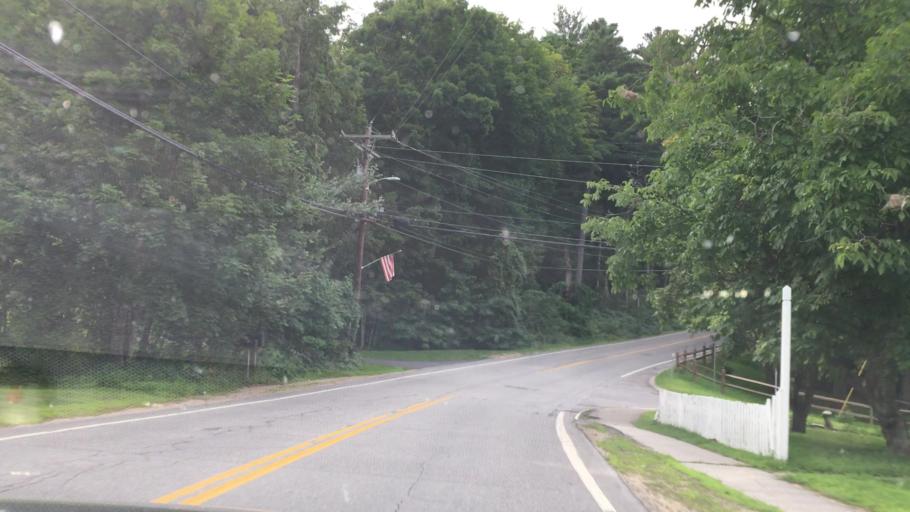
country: US
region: New Hampshire
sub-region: Carroll County
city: Center Harbor
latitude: 43.7100
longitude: -71.4658
